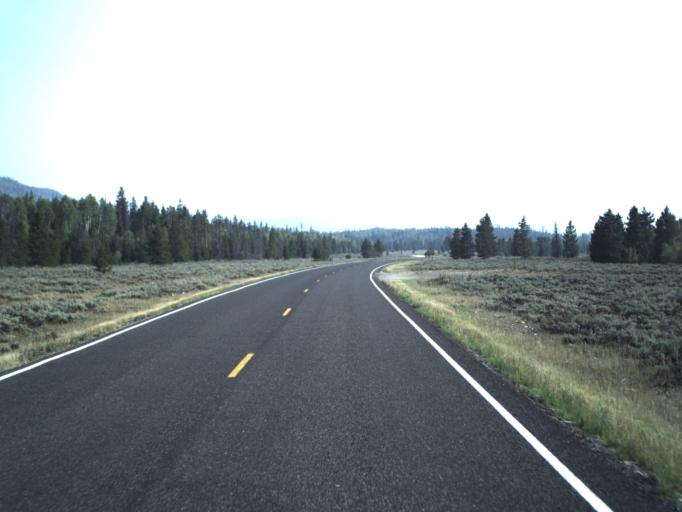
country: US
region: Wyoming
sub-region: Uinta County
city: Evanston
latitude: 40.8791
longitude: -110.8313
